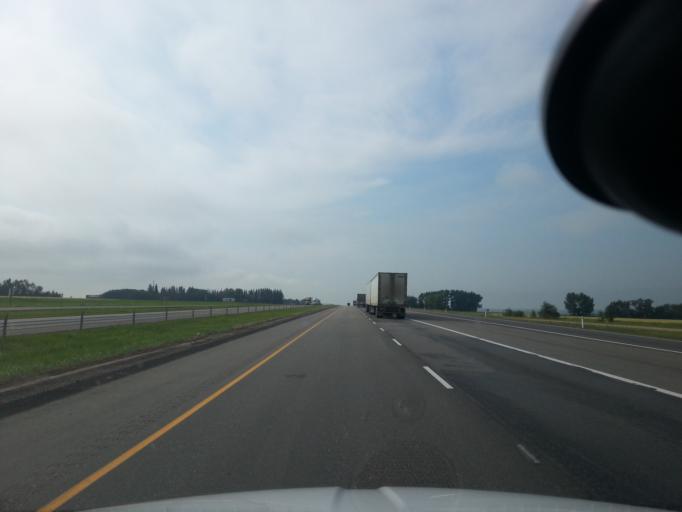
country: CA
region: Alberta
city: Penhold
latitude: 52.1396
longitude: -113.8141
